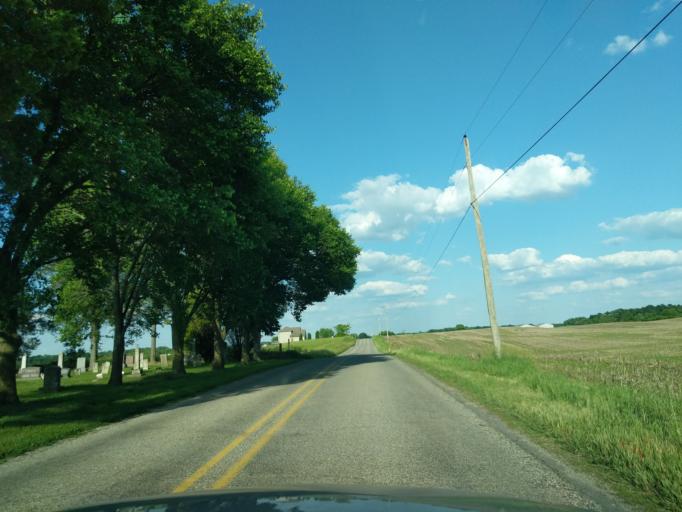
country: US
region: Indiana
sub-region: Whitley County
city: Tri-Lakes
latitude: 41.3024
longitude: -85.5415
